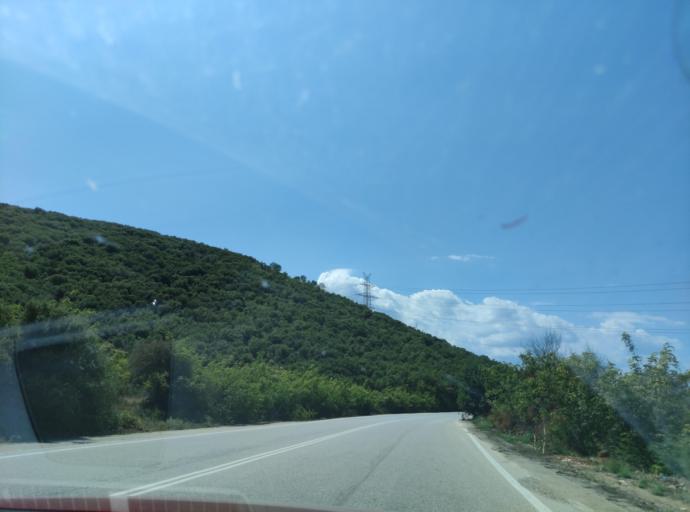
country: GR
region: East Macedonia and Thrace
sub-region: Nomos Kavalas
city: Nikisiani
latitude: 40.9876
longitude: 24.0951
